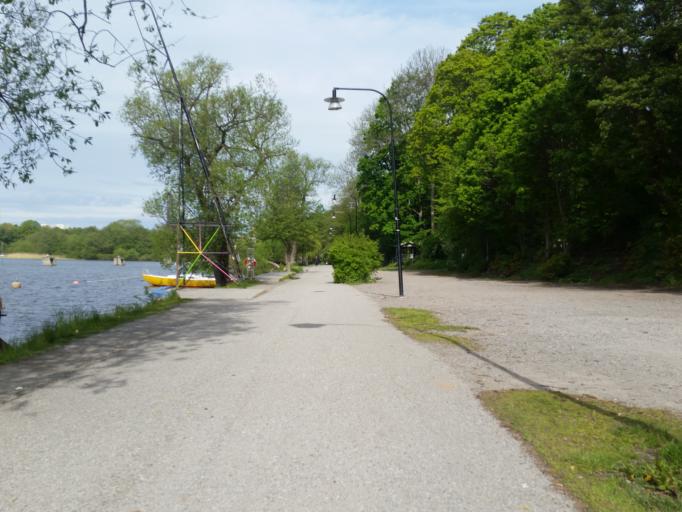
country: SE
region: Stockholm
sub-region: Stockholms Kommun
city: Arsta
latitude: 59.3071
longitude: 18.0567
